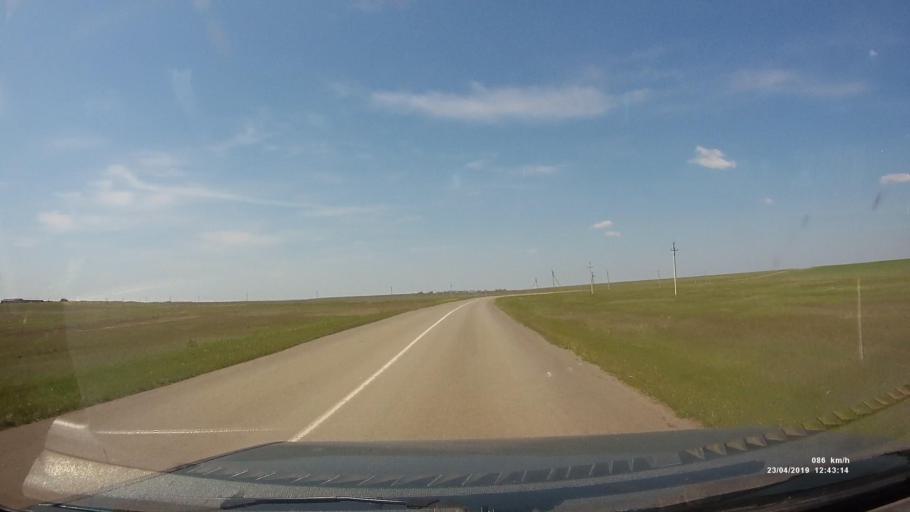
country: RU
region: Kalmykiya
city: Yashalta
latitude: 46.4624
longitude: 42.6528
